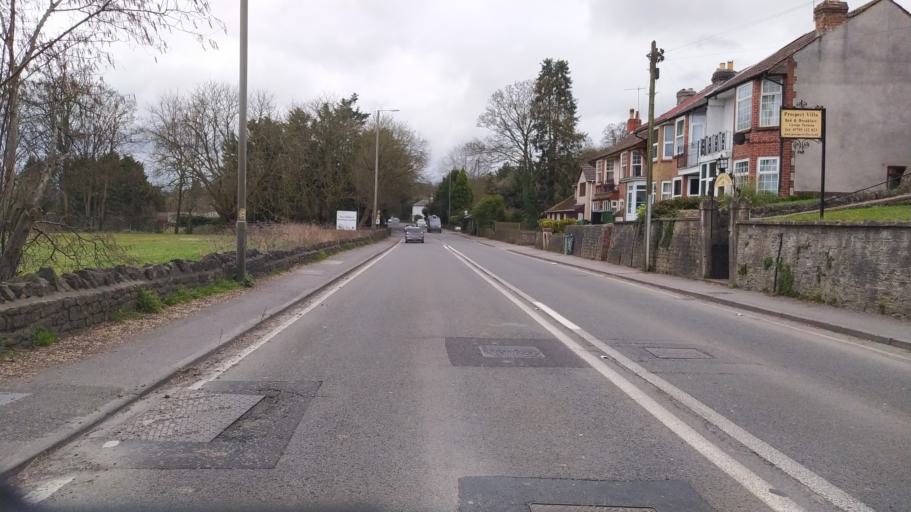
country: GB
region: England
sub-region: Bath and North East Somerset
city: Saltford
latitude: 51.3981
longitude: -2.4499
